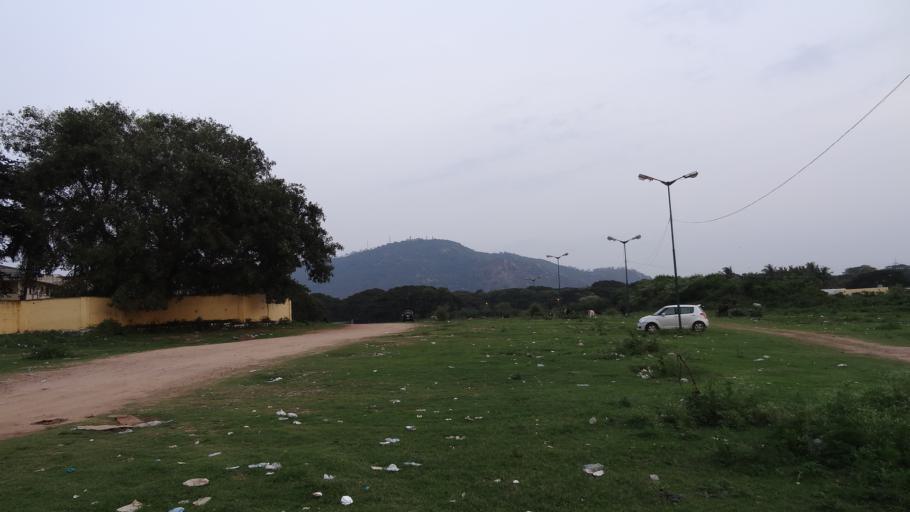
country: IN
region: Karnataka
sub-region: Mysore
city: Mysore
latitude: 12.3013
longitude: 76.6610
